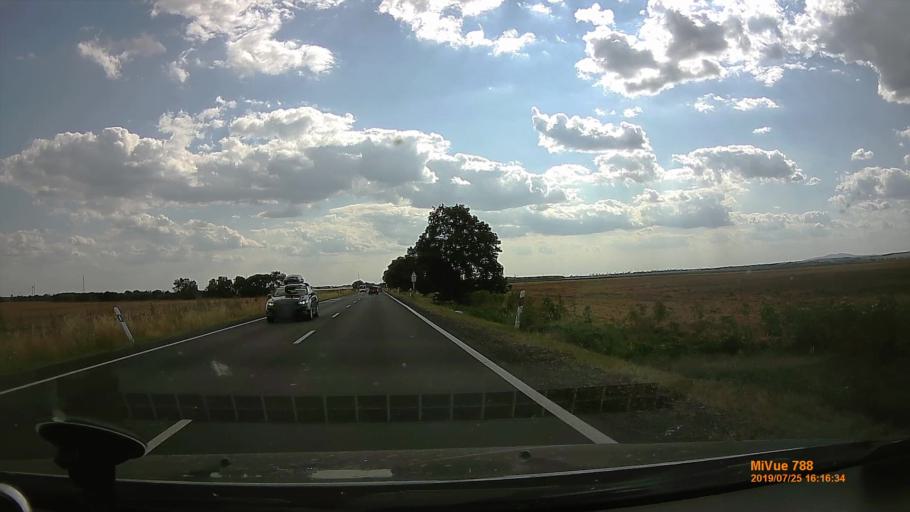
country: HU
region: Heves
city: Kal
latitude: 47.7772
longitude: 20.2893
